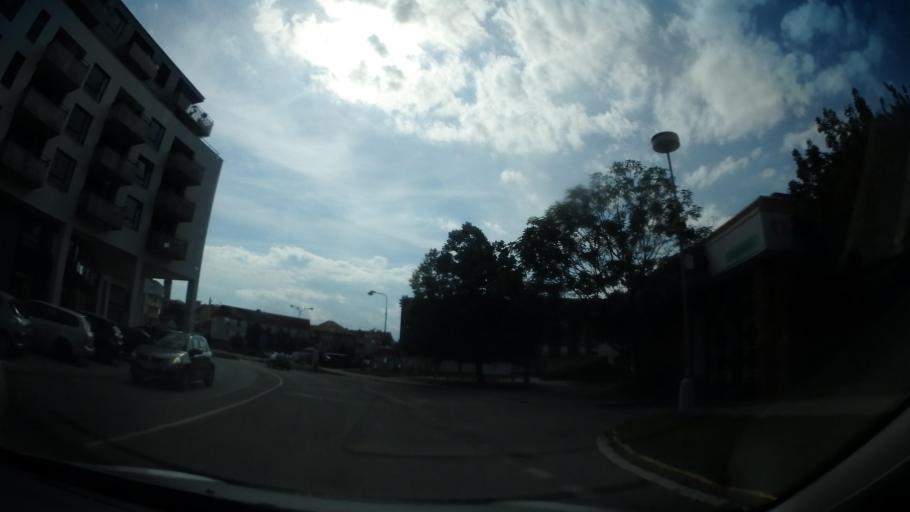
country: CZ
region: Jihocesky
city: Strakonice
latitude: 49.2585
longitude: 13.9070
